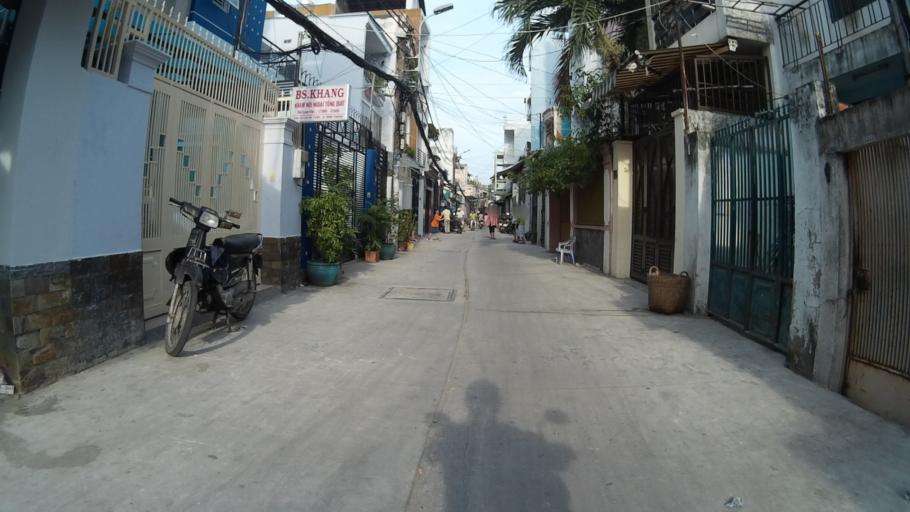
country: VN
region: Ho Chi Minh City
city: Quan Binh Thanh
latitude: 10.8012
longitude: 106.7022
